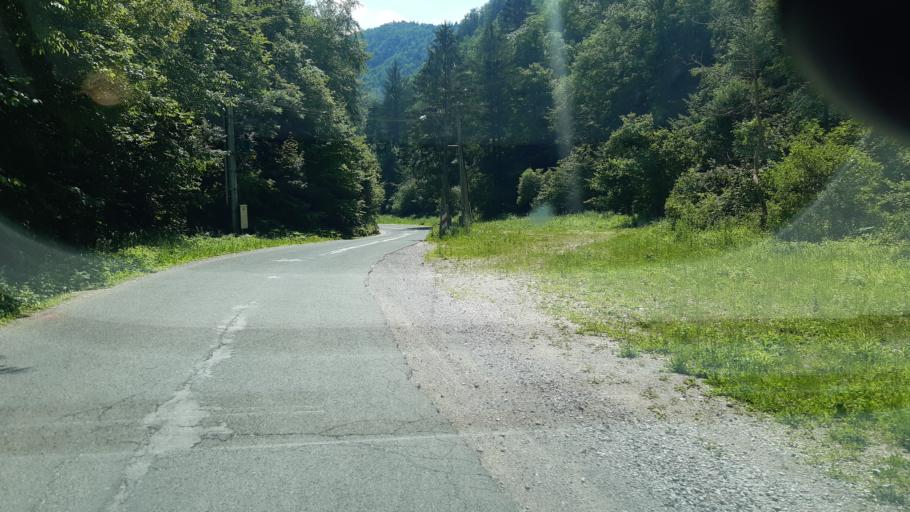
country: SI
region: Cerklje na Gorenjskem
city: Cerklje na Gorenjskem
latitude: 46.2763
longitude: 14.4959
